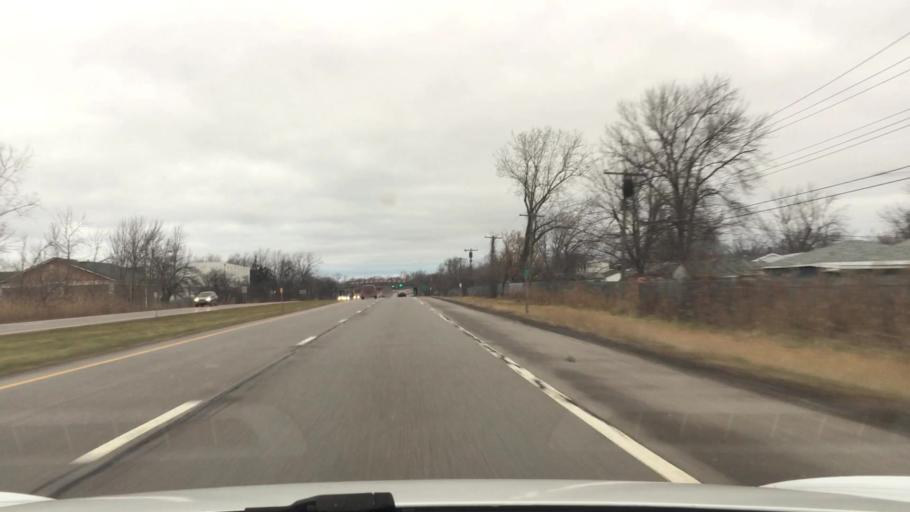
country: US
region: New York
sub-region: Erie County
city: Tonawanda
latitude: 43.0047
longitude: -78.8570
